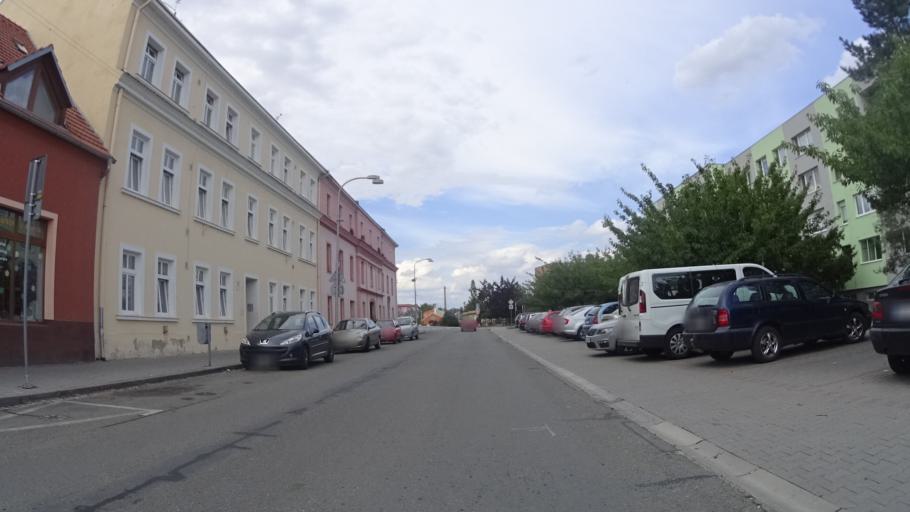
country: CZ
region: Olomoucky
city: Litovel
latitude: 49.7038
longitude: 17.0765
